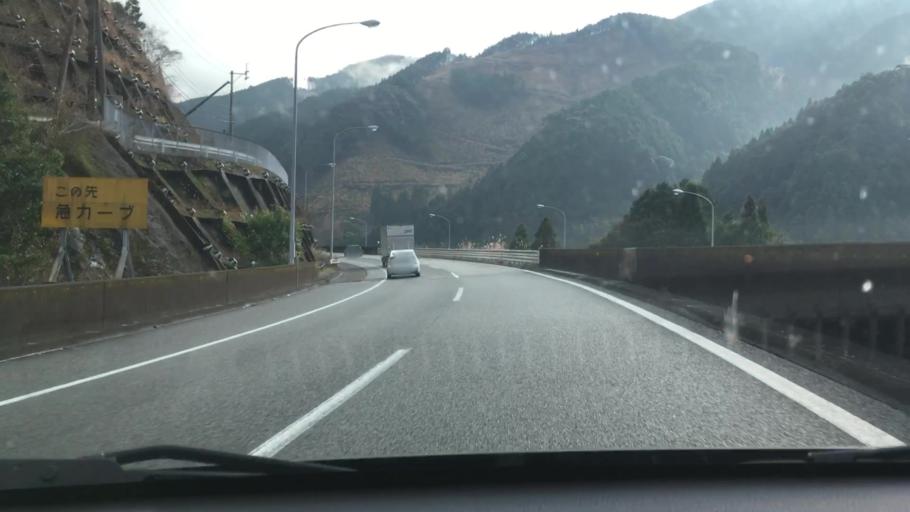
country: JP
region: Kumamoto
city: Yatsushiro
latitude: 32.4038
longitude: 130.6976
